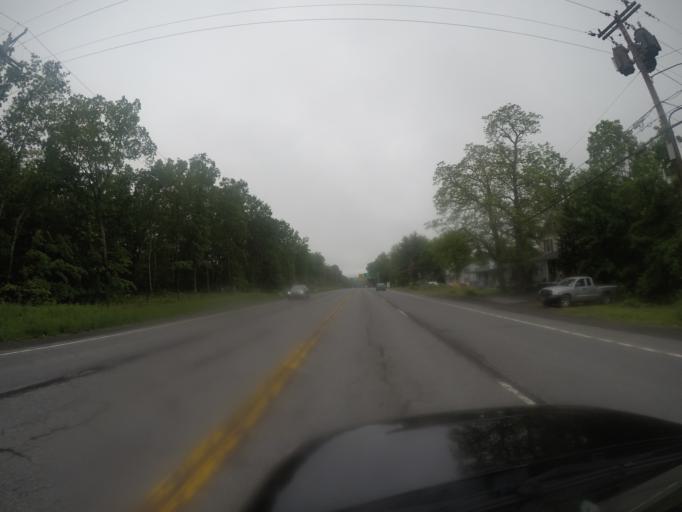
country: US
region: New York
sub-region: Ulster County
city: West Hurley
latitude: 41.9965
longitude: -74.0998
